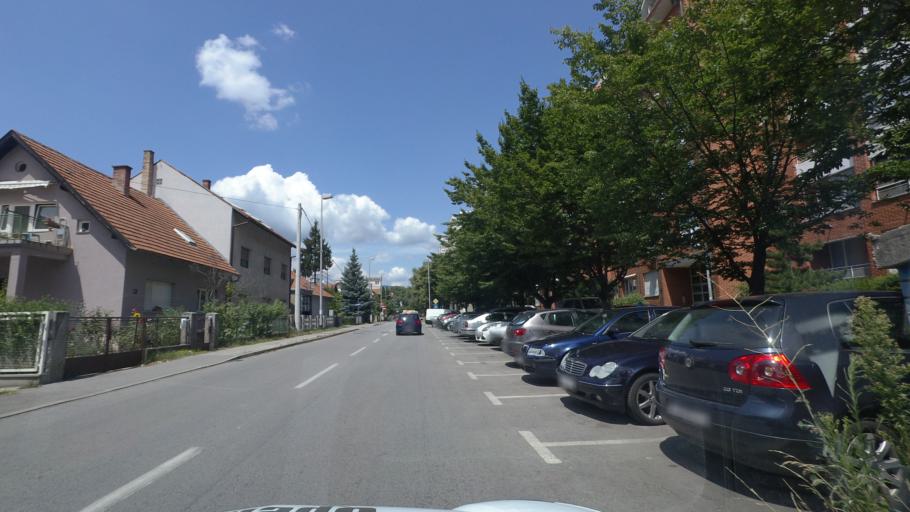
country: HR
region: Grad Zagreb
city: Dubrava
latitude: 45.8153
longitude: 16.0263
